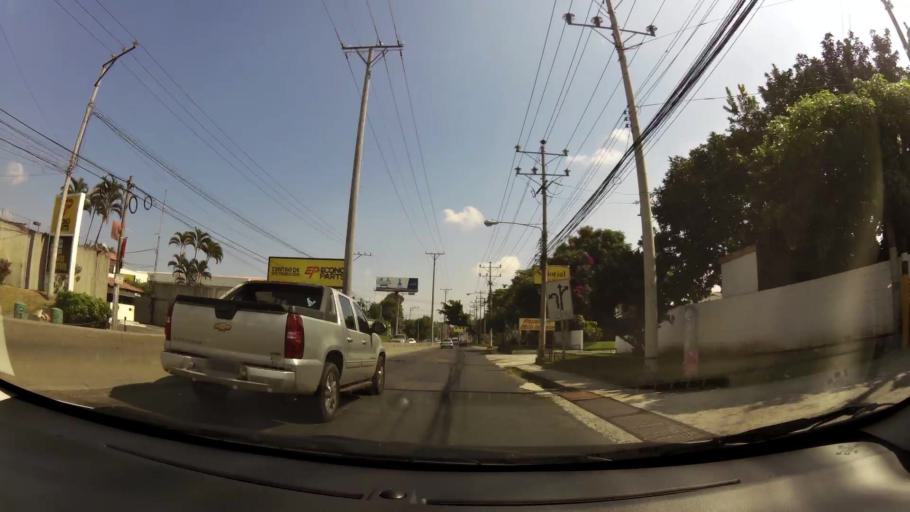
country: SV
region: La Libertad
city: Santa Tecla
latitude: 13.6683
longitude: -89.2679
